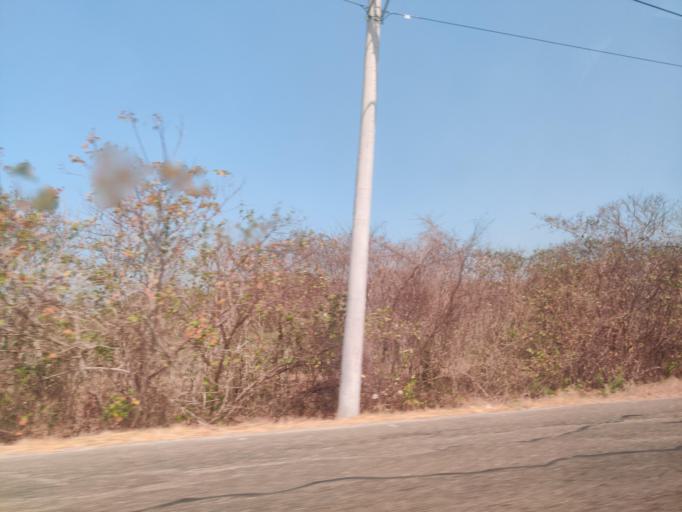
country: CO
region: Bolivar
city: Turbana
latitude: 10.2735
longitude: -75.5494
